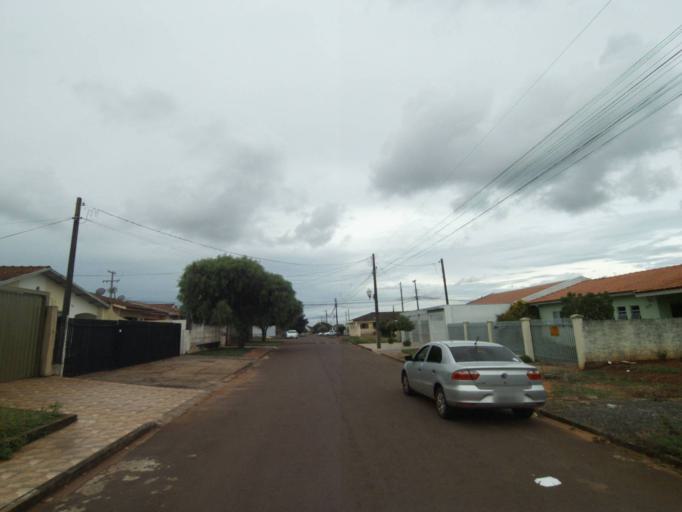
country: BR
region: Parana
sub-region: Campo Mourao
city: Campo Mourao
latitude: -24.0276
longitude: -52.3593
